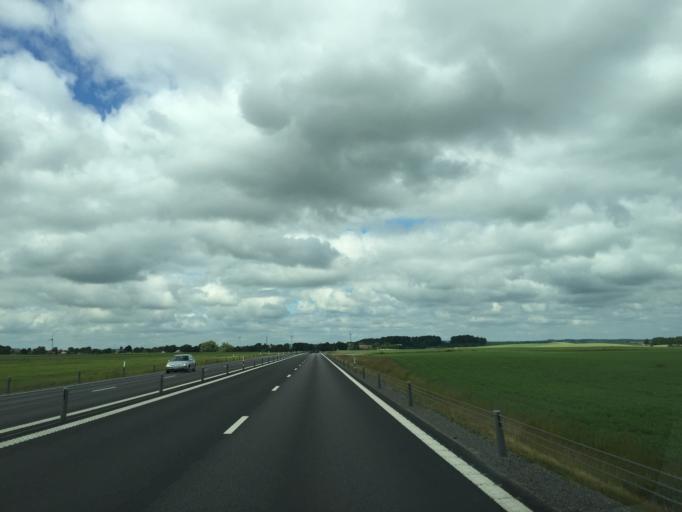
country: SE
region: Skane
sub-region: Svedala Kommun
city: Klagerup
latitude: 55.5842
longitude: 13.2539
